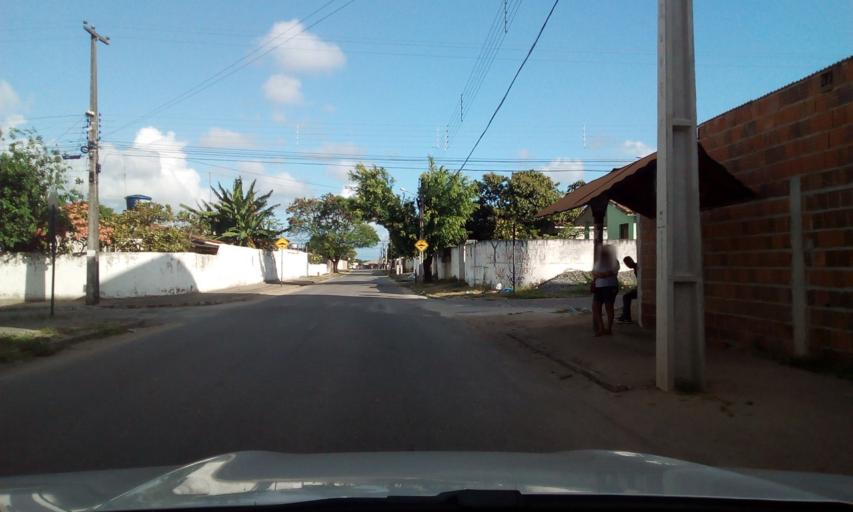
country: BR
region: Paraiba
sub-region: Bayeux
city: Bayeux
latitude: -7.1758
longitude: -34.9167
